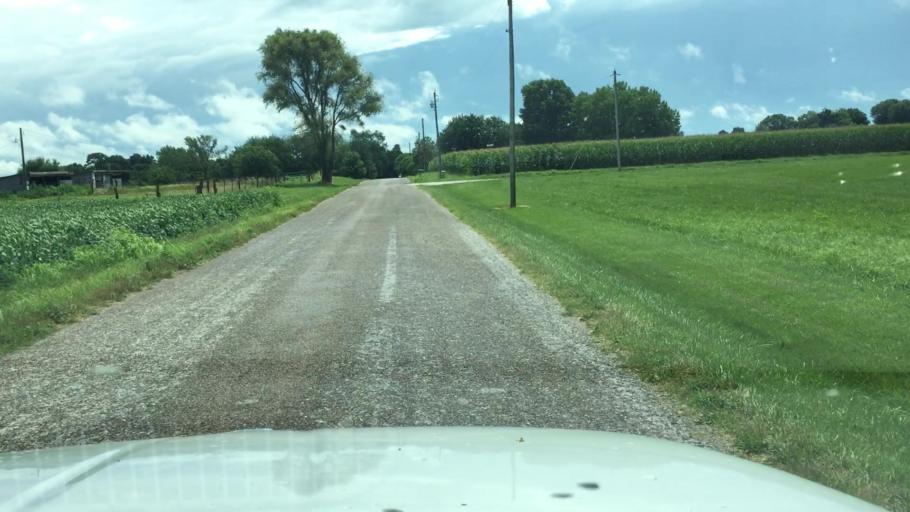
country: US
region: Illinois
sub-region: Hancock County
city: Nauvoo
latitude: 40.5427
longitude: -91.3651
